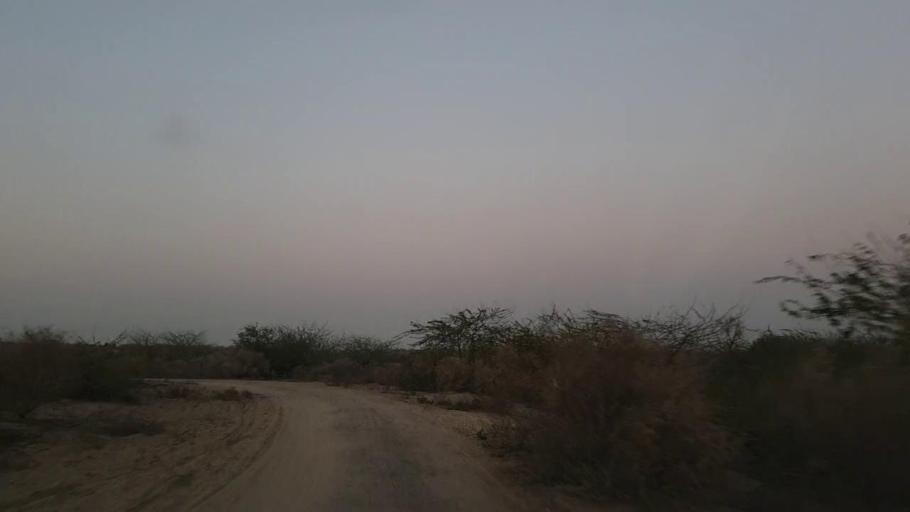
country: PK
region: Sindh
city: Bandhi
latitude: 26.6099
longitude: 68.3897
